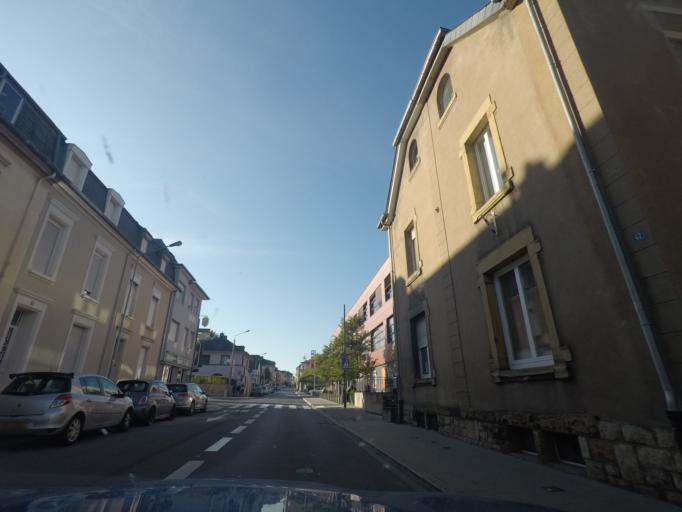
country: LU
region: Luxembourg
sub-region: Canton de Luxembourg
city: Luxembourg
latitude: 49.5948
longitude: 6.1404
